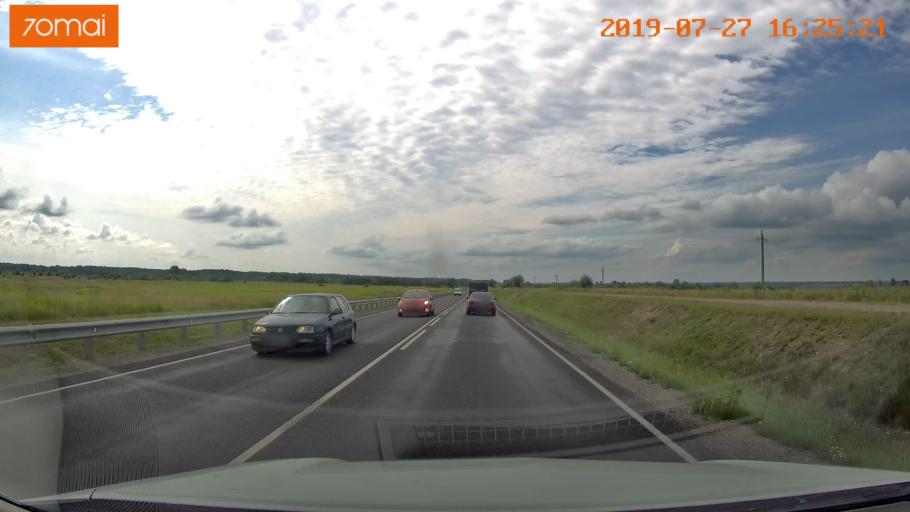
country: RU
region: Kaliningrad
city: Zheleznodorozhnyy
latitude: 54.6370
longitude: 21.4331
